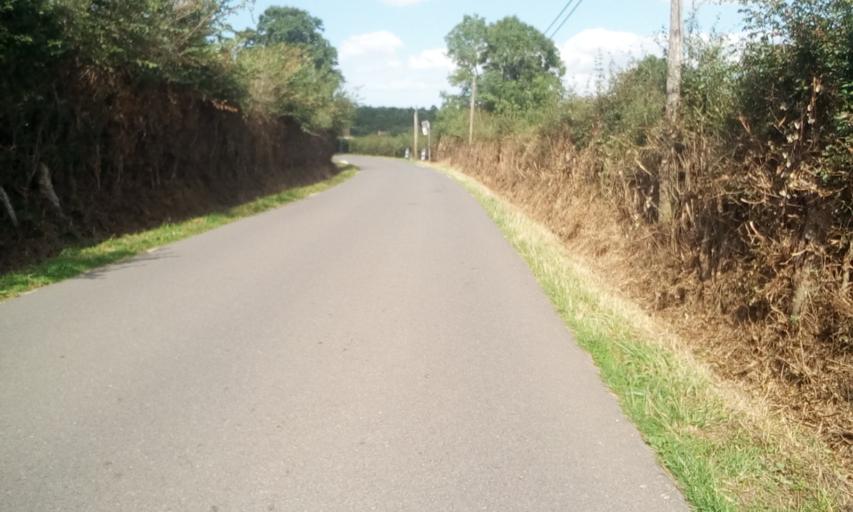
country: FR
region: Lower Normandy
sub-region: Departement du Calvados
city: Argences
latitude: 49.1294
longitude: -0.1309
